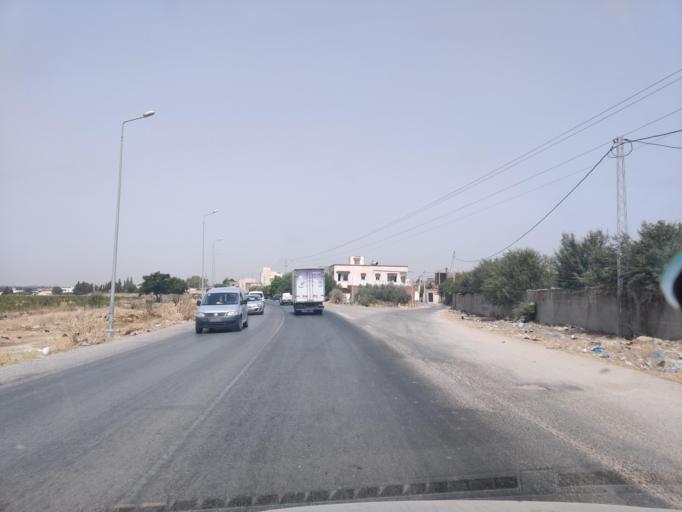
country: TN
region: Tunis
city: La Sebala du Mornag
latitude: 36.6579
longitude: 10.3307
